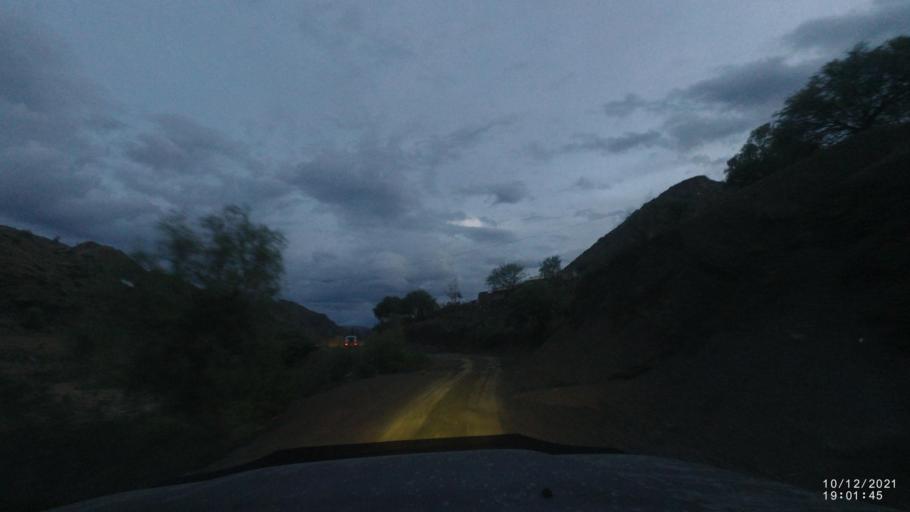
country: BO
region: Cochabamba
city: Tarata
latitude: -17.8981
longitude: -65.9456
